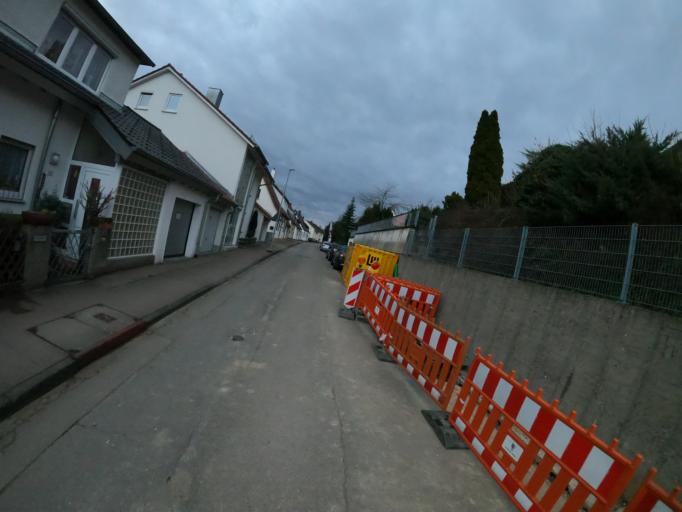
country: DE
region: Baden-Wuerttemberg
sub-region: Regierungsbezirk Stuttgart
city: Wangen
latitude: 48.7117
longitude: 9.6288
